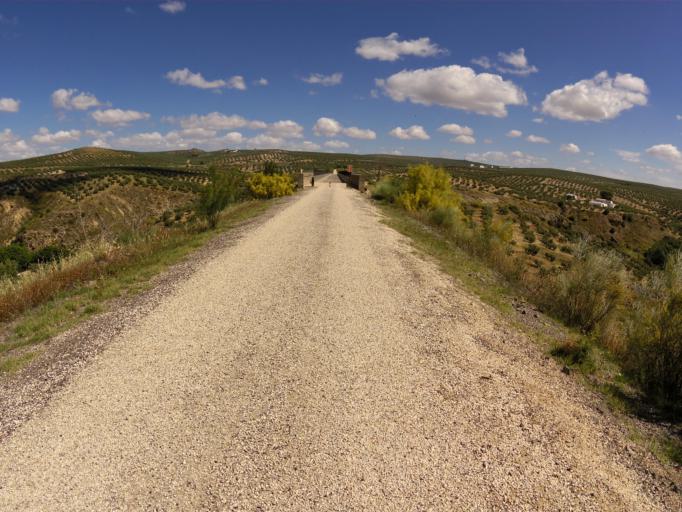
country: ES
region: Andalusia
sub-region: Provincia de Jaen
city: Alcaudete
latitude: 37.6359
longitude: -4.0824
